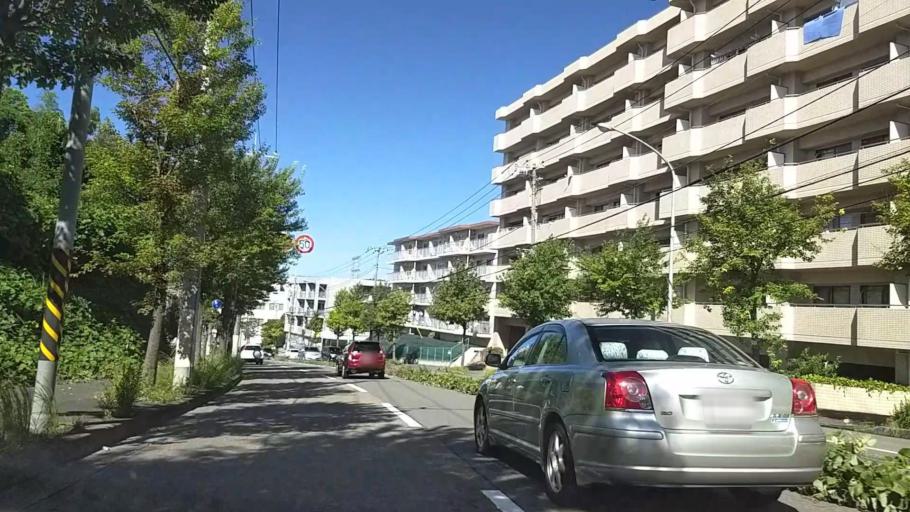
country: JP
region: Tokyo
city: Chofugaoka
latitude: 35.5709
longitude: 139.5569
